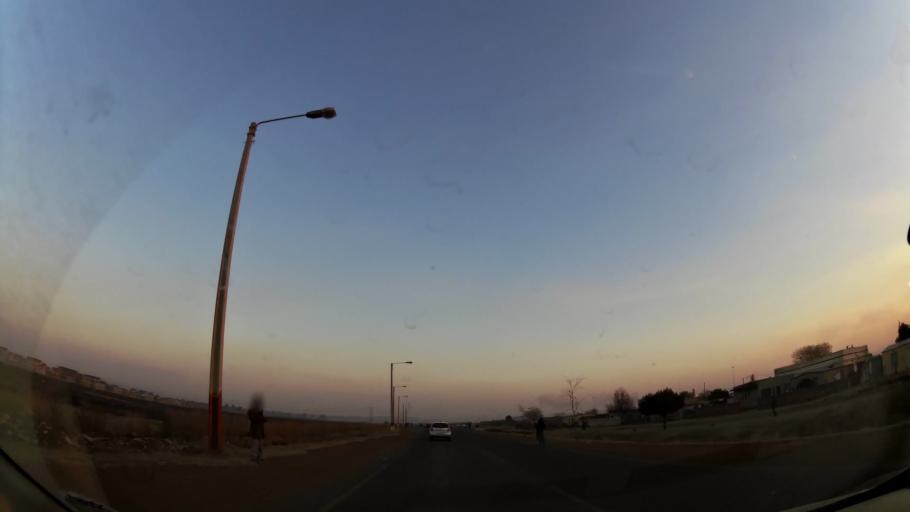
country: ZA
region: Gauteng
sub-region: Ekurhuleni Metropolitan Municipality
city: Springs
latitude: -26.3135
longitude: 28.4259
